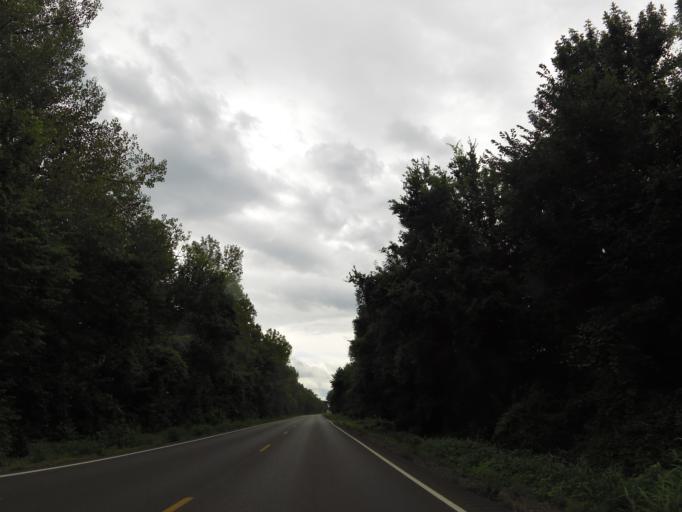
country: US
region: Kentucky
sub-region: Ballard County
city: Wickliffe
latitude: 36.9921
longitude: -89.1146
